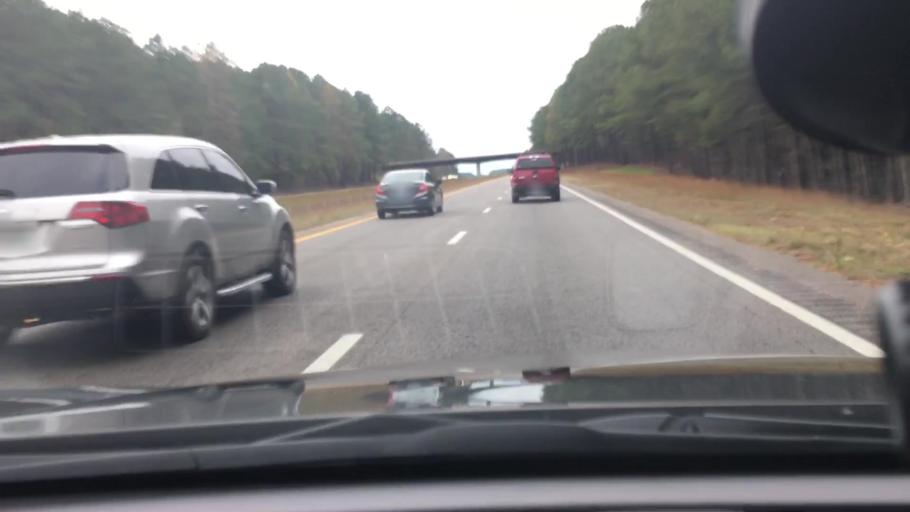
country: US
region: North Carolina
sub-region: Wake County
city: Zebulon
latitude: 35.8137
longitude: -78.2370
